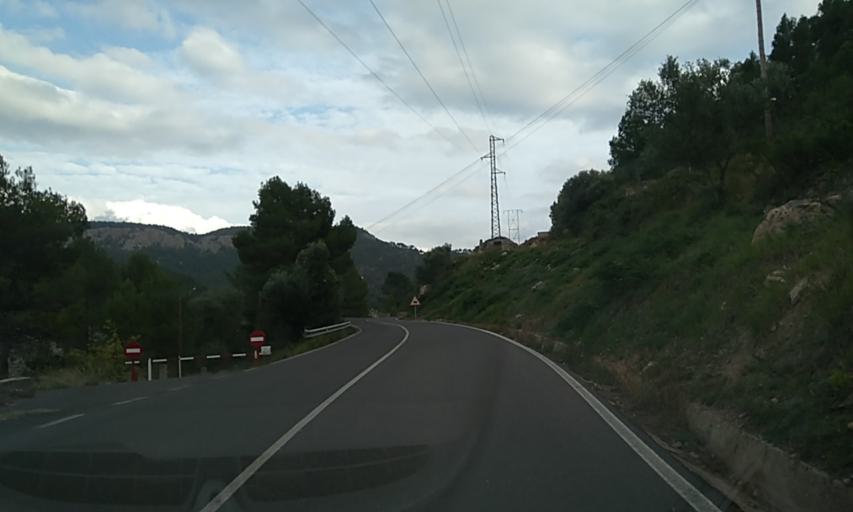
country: ES
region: Valencia
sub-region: Provincia de Castello
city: Puebla de Arenoso
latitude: 40.0847
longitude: -0.5524
